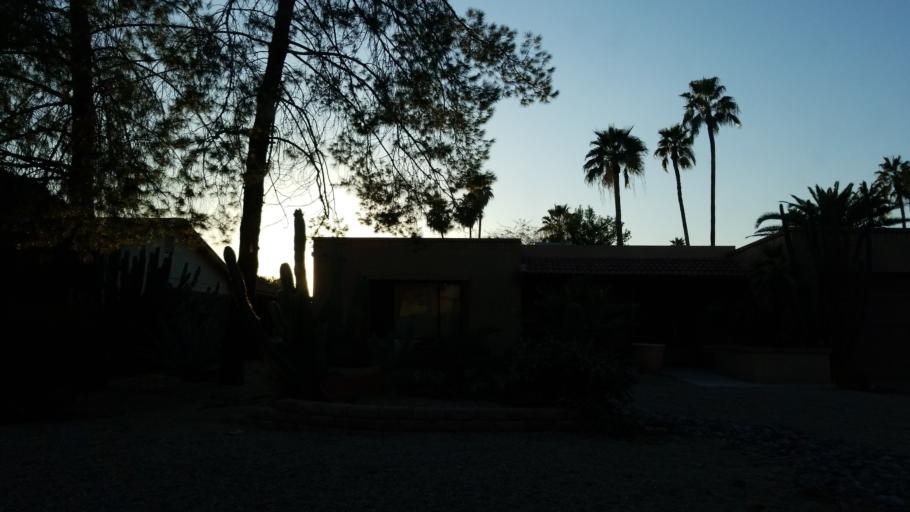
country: US
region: Arizona
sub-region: Maricopa County
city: Paradise Valley
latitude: 33.6070
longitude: -111.9736
